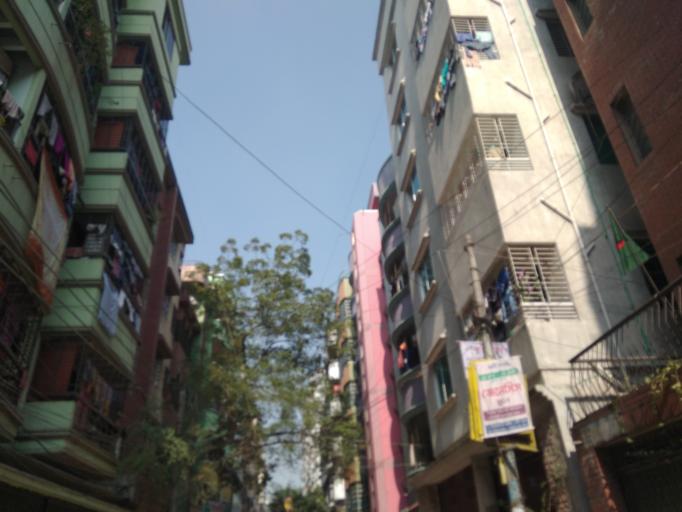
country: BD
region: Dhaka
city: Azimpur
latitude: 23.7629
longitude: 90.3573
